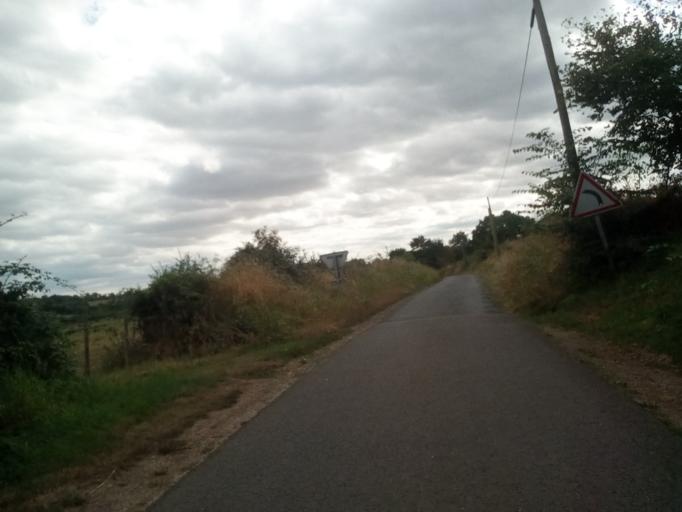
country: FR
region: Lower Normandy
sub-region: Departement du Calvados
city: Troarn
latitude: 49.1635
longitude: -0.1527
